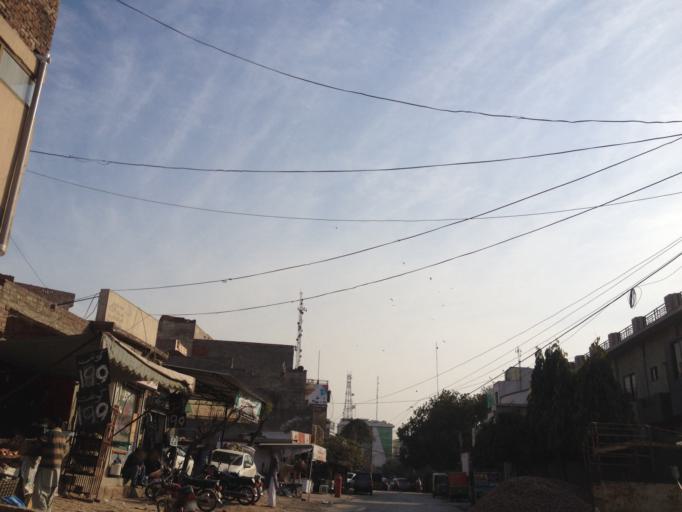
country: PK
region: Punjab
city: Lahore
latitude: 31.5035
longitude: 74.3189
